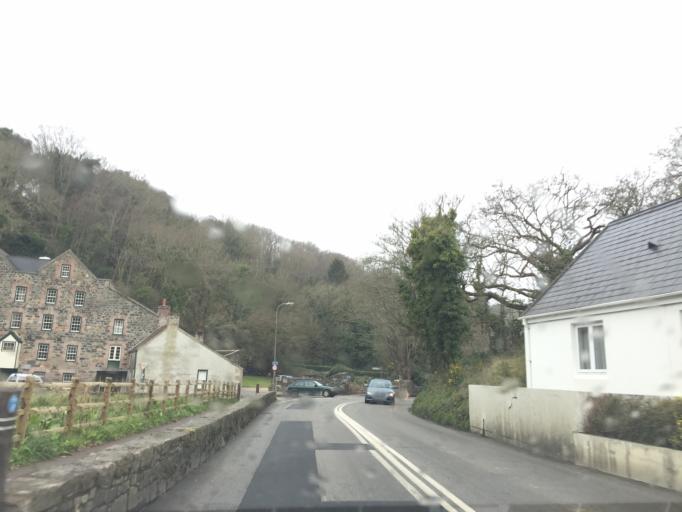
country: JE
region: St Helier
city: Saint Helier
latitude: 49.2049
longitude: -2.1551
